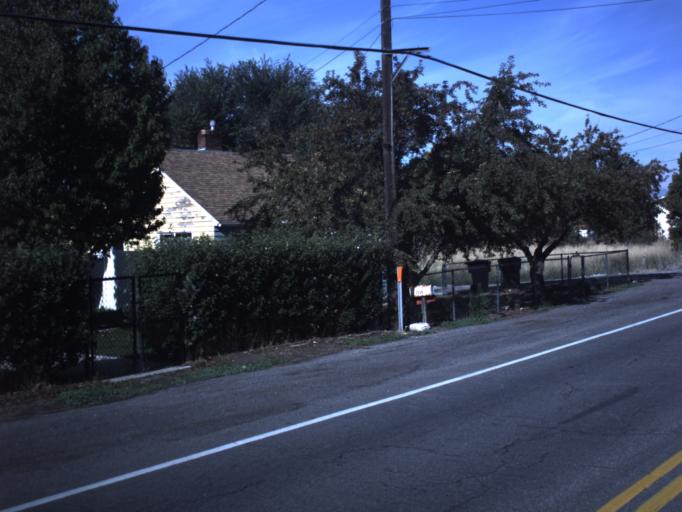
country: US
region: Utah
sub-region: Utah County
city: Provo
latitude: 40.2480
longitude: -111.7010
